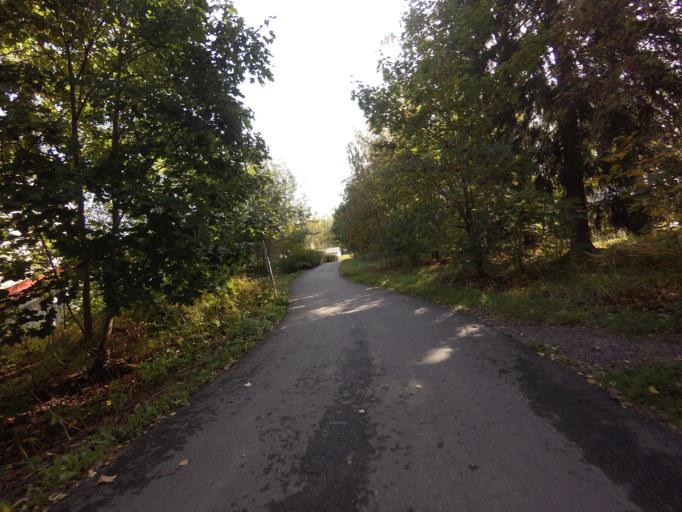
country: FI
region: Uusimaa
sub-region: Helsinki
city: Espoo
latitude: 60.1787
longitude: 24.6551
